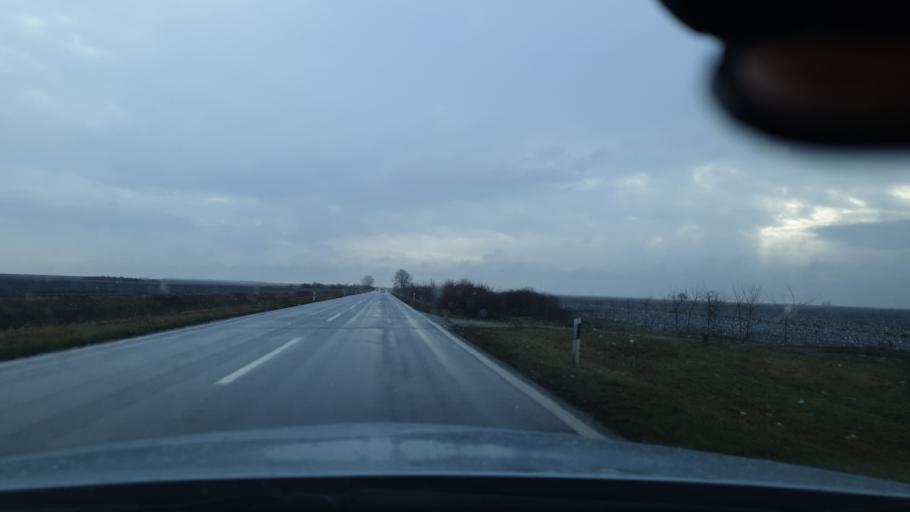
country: RS
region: Autonomna Pokrajina Vojvodina
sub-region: Juznobanatski Okrug
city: Pancevo
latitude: 44.8410
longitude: 20.7986
